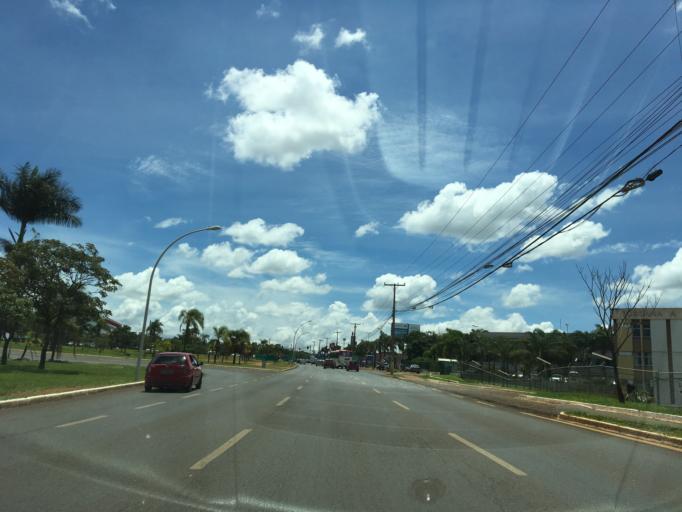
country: BR
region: Federal District
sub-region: Brasilia
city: Brasilia
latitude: -15.7335
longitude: -47.8968
